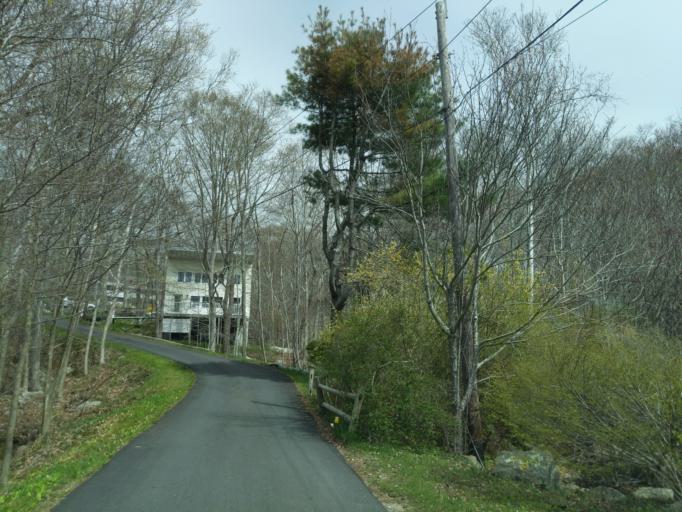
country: US
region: Massachusetts
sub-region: Essex County
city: Rockport
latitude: 42.6379
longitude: -70.6048
